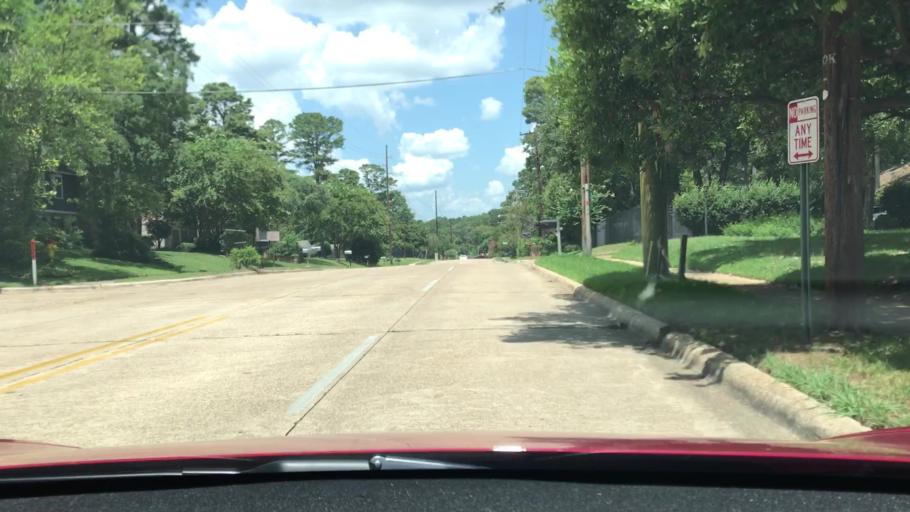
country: US
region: Louisiana
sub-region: Bossier Parish
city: Bossier City
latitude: 32.4400
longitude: -93.7362
